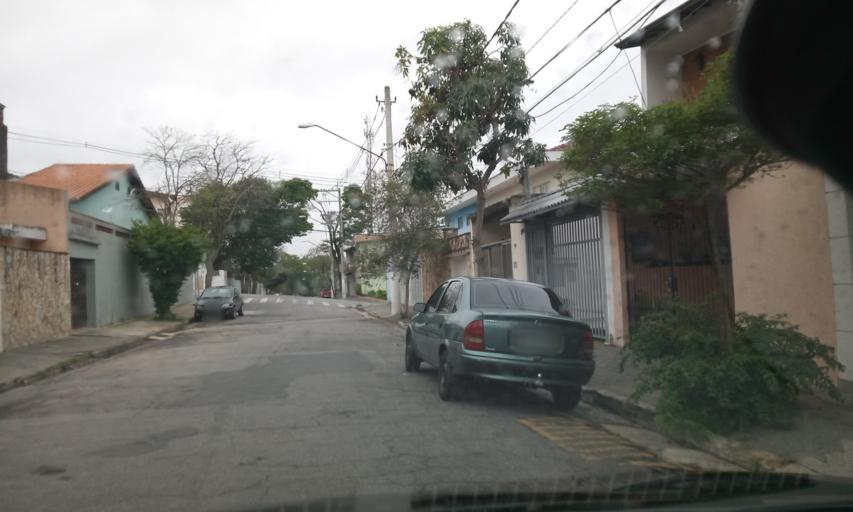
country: BR
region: Sao Paulo
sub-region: Sao Bernardo Do Campo
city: Sao Bernardo do Campo
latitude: -23.6758
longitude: -46.5602
